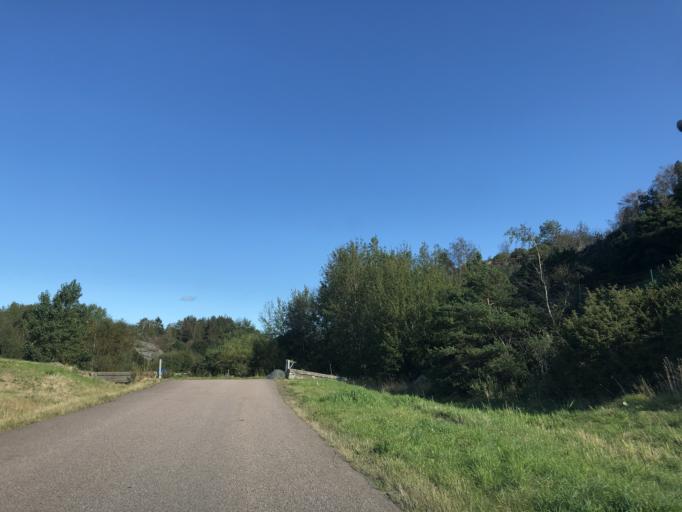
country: SE
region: Vaestra Goetaland
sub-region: Goteborg
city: Torslanda
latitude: 57.7163
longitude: 11.8087
